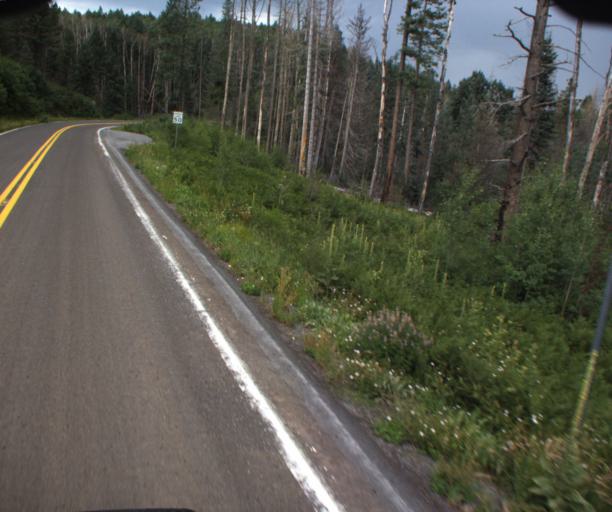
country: US
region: Arizona
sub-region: Greenlee County
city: Morenci
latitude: 33.5682
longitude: -109.3565
